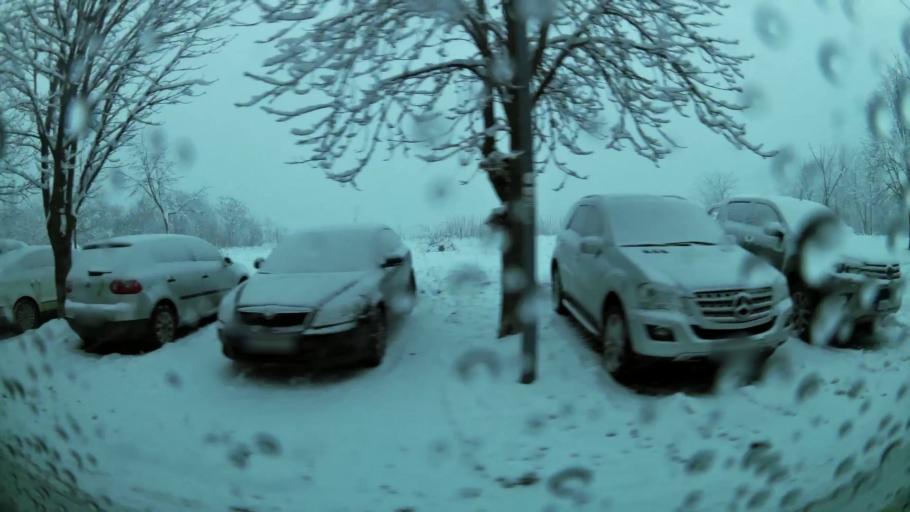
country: RS
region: Central Serbia
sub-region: Belgrade
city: Zemun
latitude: 44.8142
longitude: 20.3851
